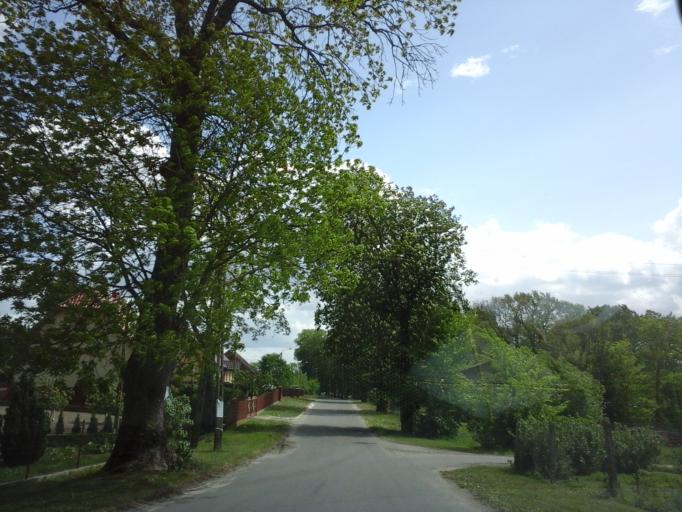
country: PL
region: West Pomeranian Voivodeship
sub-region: Powiat choszczenski
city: Choszczno
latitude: 53.1082
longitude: 15.4052
